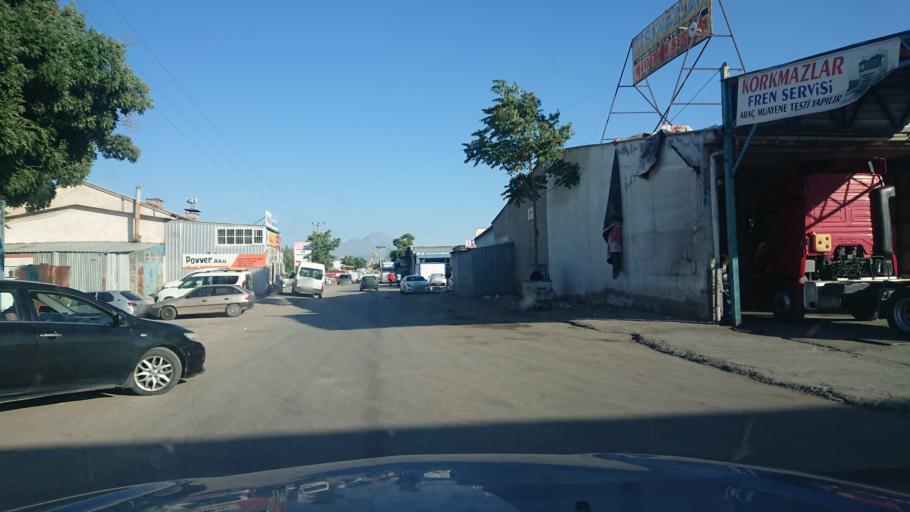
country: TR
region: Aksaray
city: Aksaray
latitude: 38.3769
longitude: 33.9908
